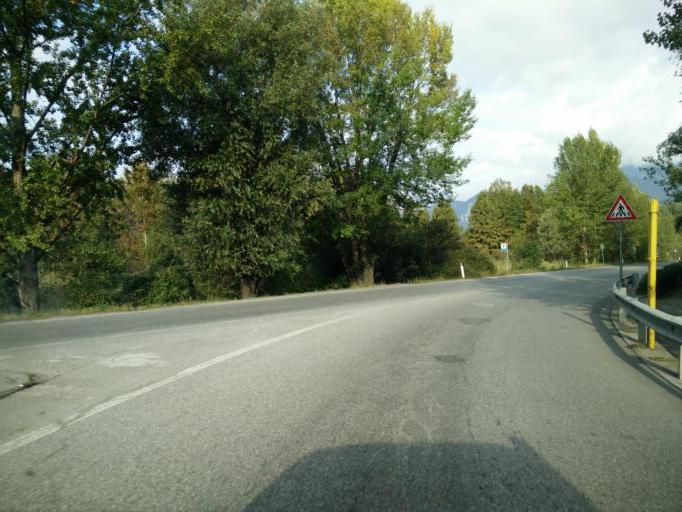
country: IT
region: Lombardy
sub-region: Provincia di Brescia
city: Iseo
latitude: 45.6512
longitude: 10.0410
